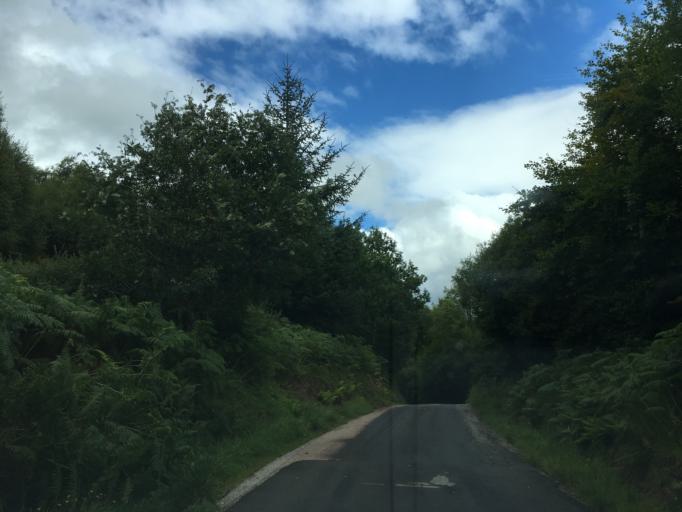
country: GB
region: Scotland
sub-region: Argyll and Bute
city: Oban
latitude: 56.3487
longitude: -5.1844
